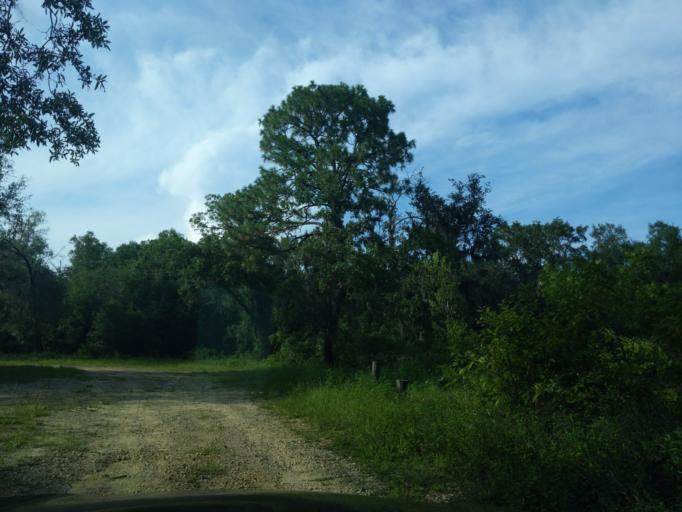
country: US
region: Florida
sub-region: Gadsden County
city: Midway
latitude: 30.3918
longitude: -84.4084
